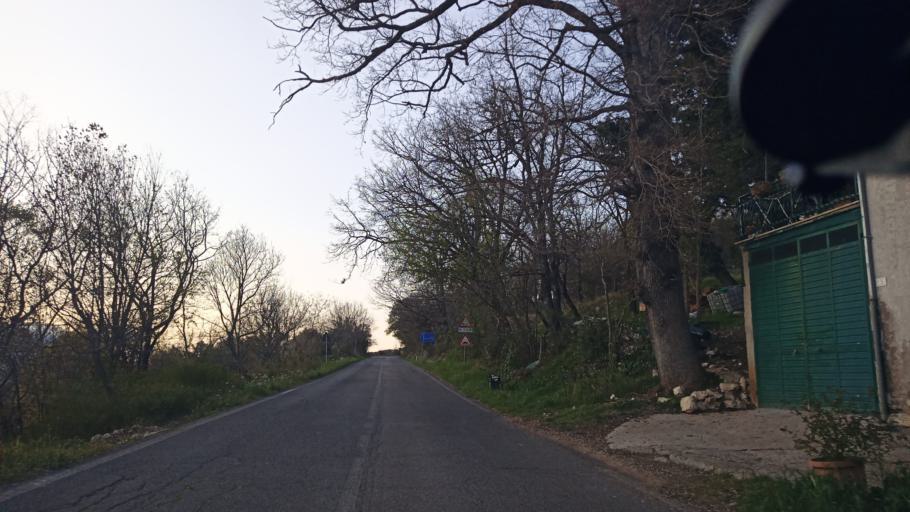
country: IT
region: Latium
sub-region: Provincia di Rieti
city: Cottanello
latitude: 42.4110
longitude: 12.6798
